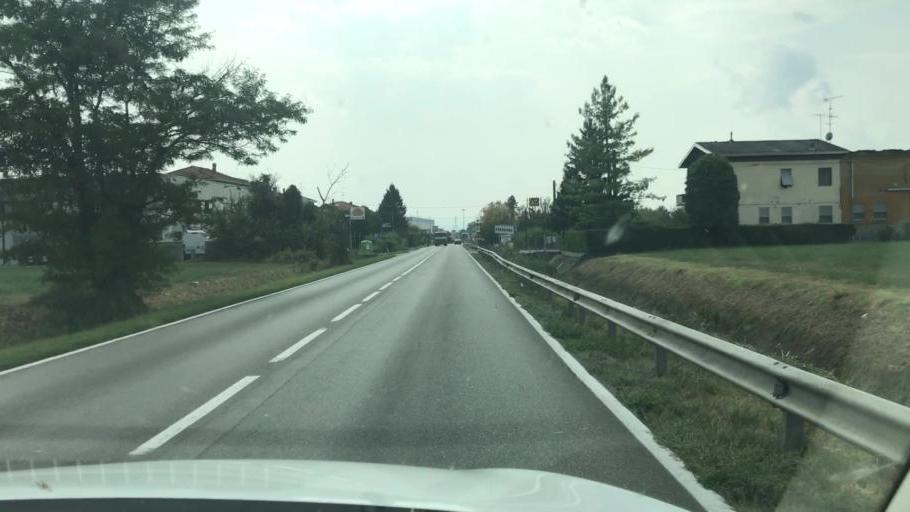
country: IT
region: Emilia-Romagna
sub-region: Provincia di Parma
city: Baganzola
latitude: 44.8544
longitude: 10.3428
